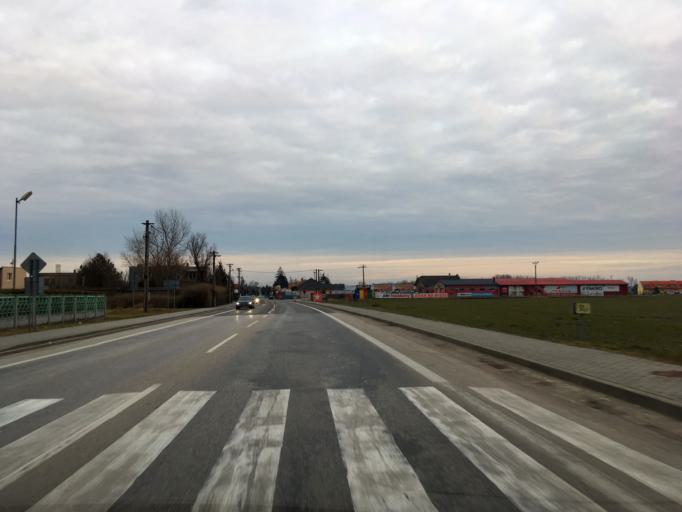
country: SK
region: Trnavsky
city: Dunajska Streda
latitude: 47.9790
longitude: 17.6547
